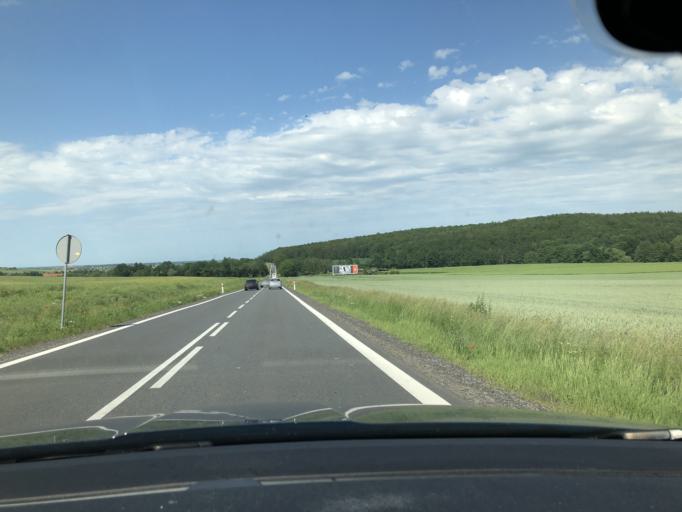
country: PL
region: Lower Silesian Voivodeship
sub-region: Powiat jaworski
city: Paszowice
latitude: 50.9575
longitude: 16.1442
